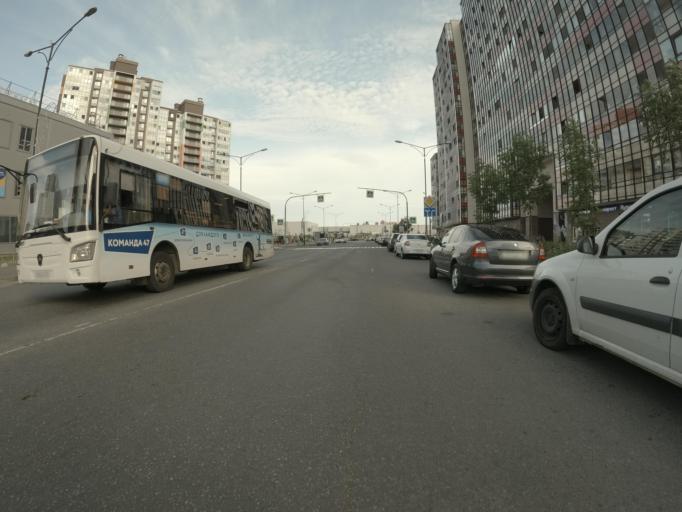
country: RU
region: Leningrad
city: Rybatskoye
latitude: 59.8983
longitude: 30.5120
